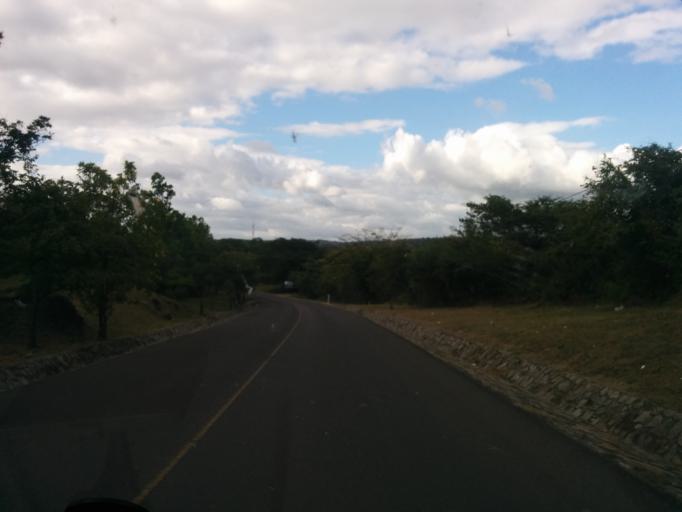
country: NI
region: Esteli
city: Esteli
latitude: 13.1749
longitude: -86.3668
